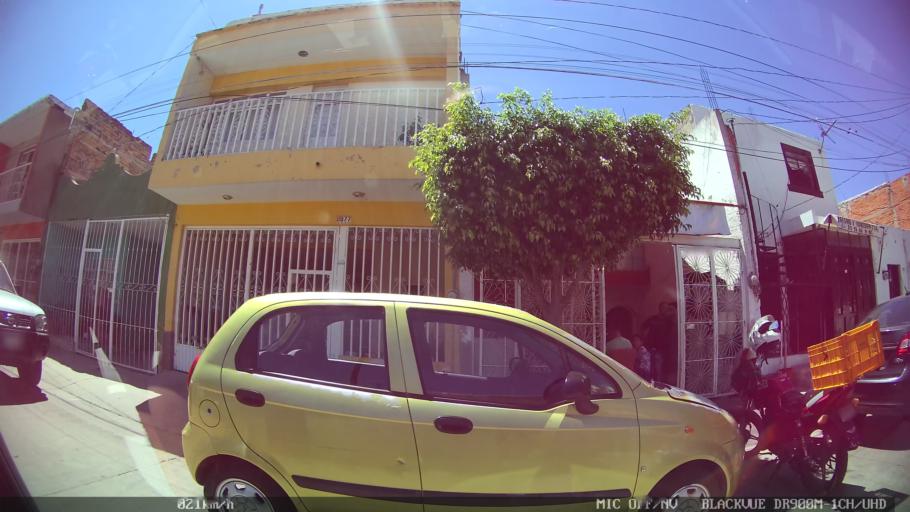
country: MX
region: Jalisco
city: Tlaquepaque
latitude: 20.6747
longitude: -103.2748
